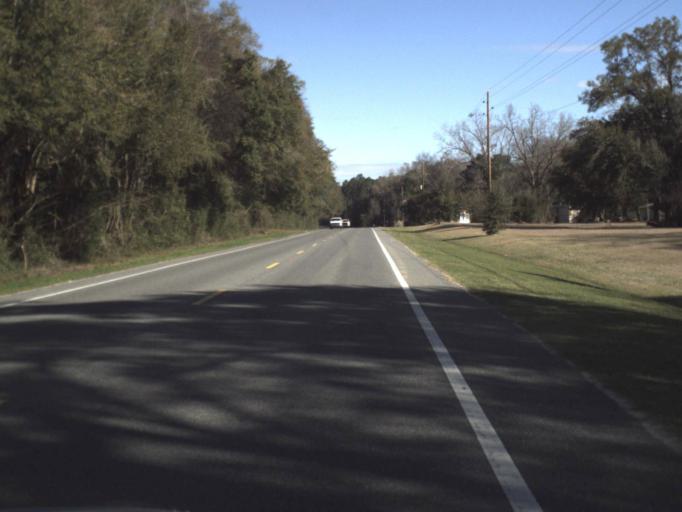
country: US
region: Florida
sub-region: Jackson County
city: Malone
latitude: 30.9174
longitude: -85.1607
